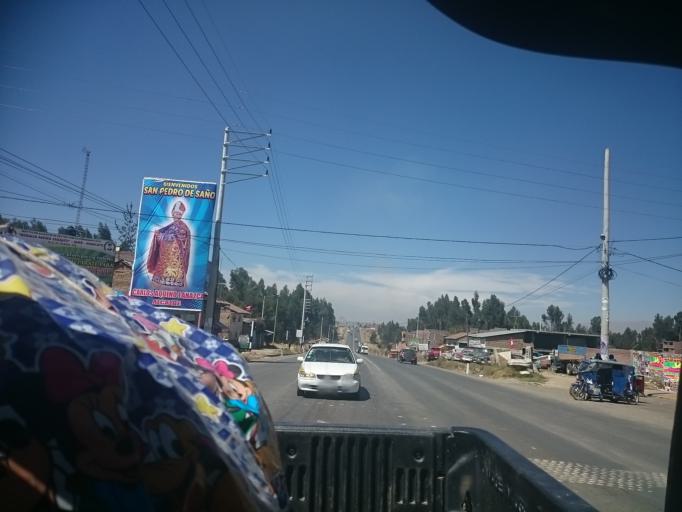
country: PE
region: Junin
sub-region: Provincia de Huancayo
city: San Agustin
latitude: -11.9689
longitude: -75.2698
